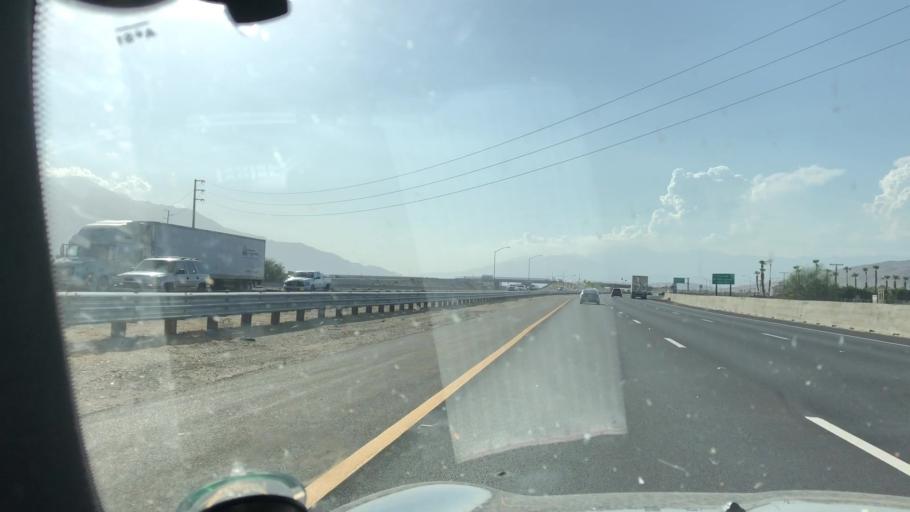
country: US
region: California
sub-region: Riverside County
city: Thousand Palms
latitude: 33.8014
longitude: -116.3805
